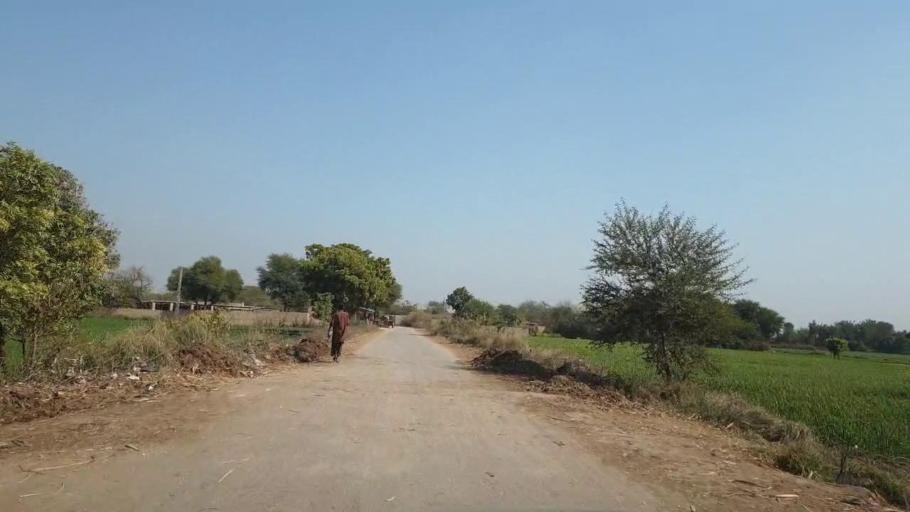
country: PK
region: Sindh
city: Tando Allahyar
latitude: 25.5645
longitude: 68.7061
